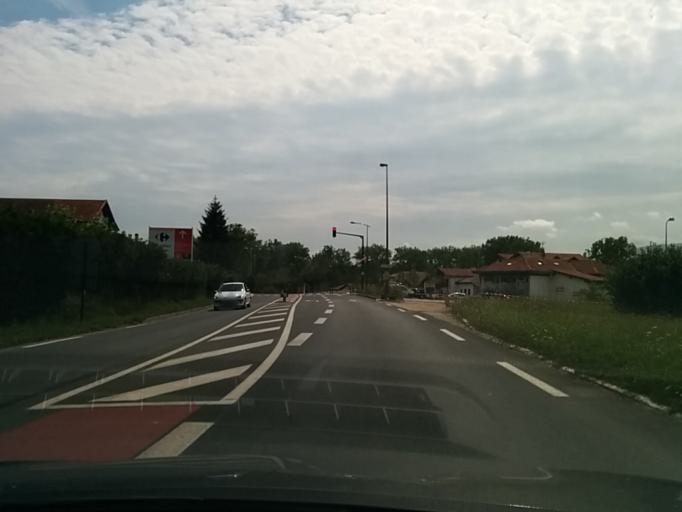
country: FR
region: Aquitaine
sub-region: Departement des Pyrenees-Atlantiques
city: Urrugne
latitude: 43.3609
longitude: -1.7013
